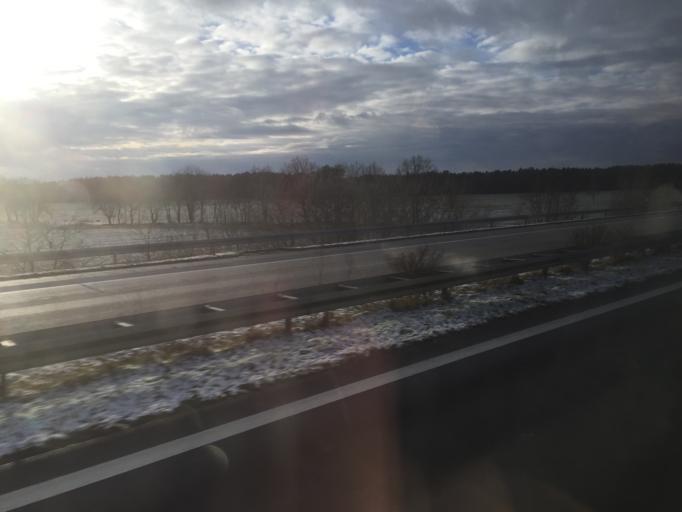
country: DE
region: Mecklenburg-Vorpommern
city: Locknitz
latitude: 53.3371
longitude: 11.8532
